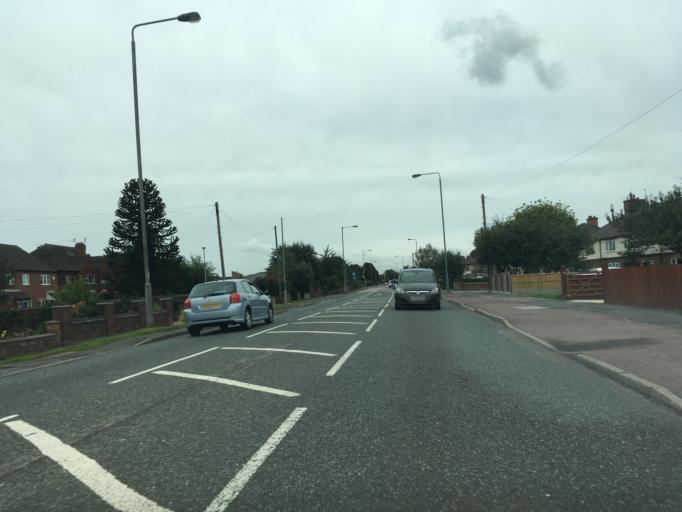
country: GB
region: England
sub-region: Nottinghamshire
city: Newark on Trent
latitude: 53.0885
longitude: -0.7943
